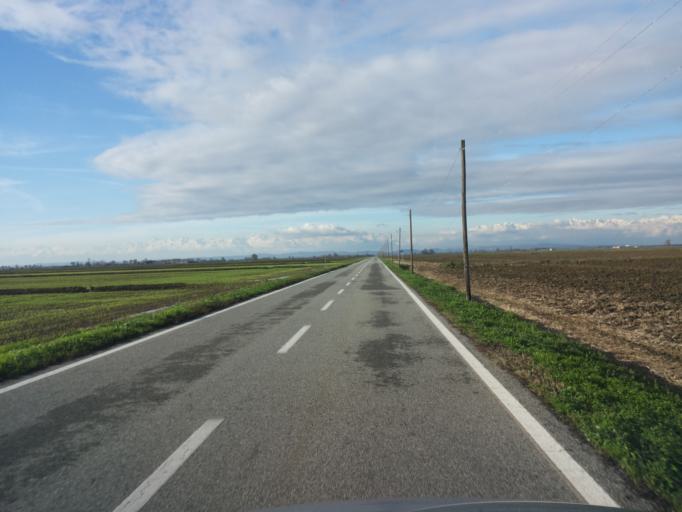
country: IT
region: Piedmont
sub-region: Provincia di Vercelli
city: Salasco
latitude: 45.2872
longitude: 8.2353
